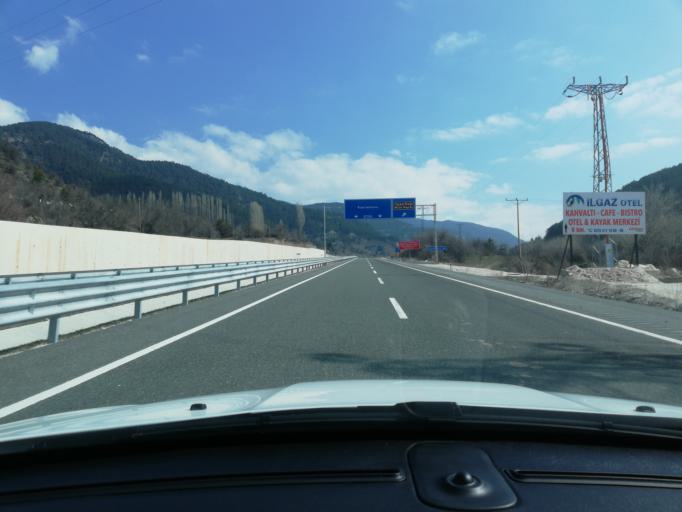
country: TR
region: Cankiri
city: Ilgaz
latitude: 41.0224
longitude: 33.7138
